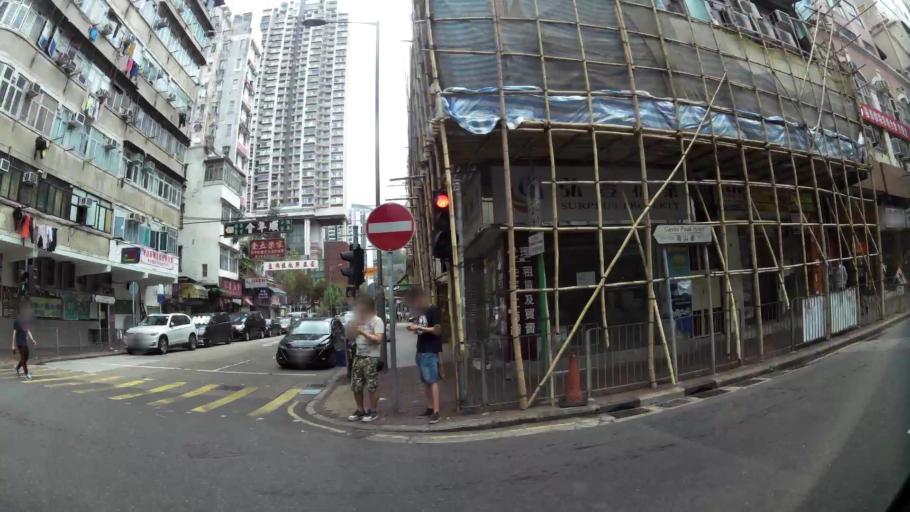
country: HK
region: Sham Shui Po
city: Sham Shui Po
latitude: 22.3356
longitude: 114.1600
